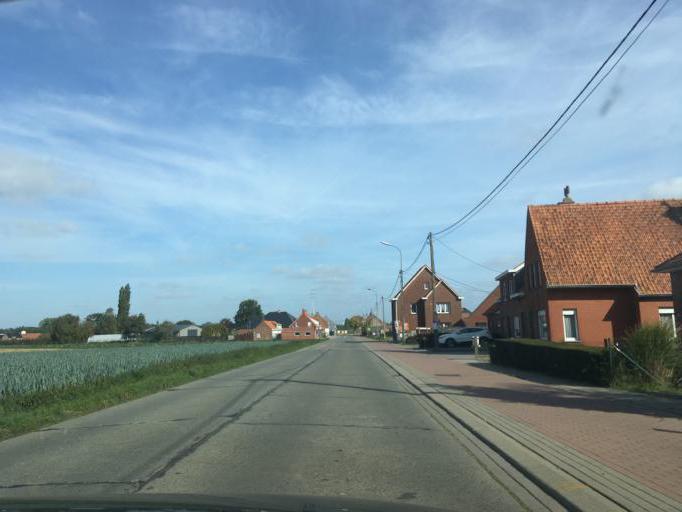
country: BE
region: Flanders
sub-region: Provincie West-Vlaanderen
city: Moorslede
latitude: 50.9109
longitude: 3.0761
